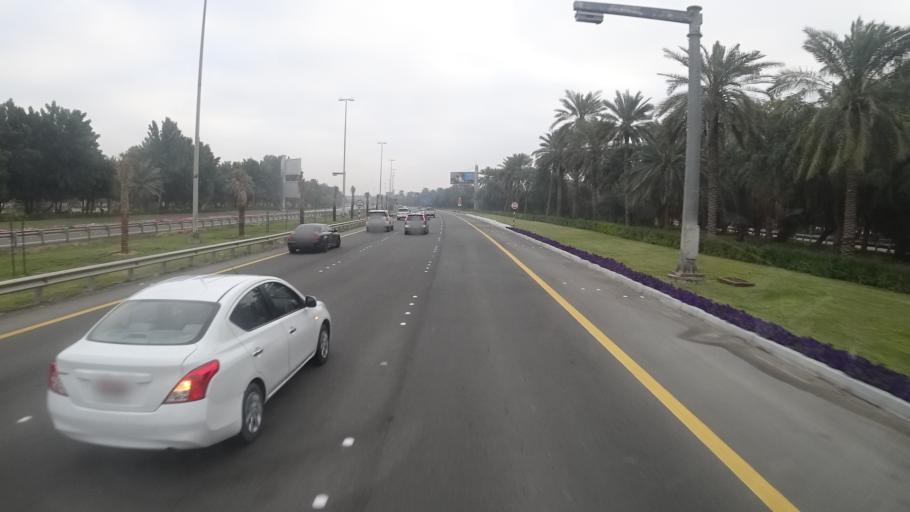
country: AE
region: Abu Dhabi
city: Abu Dhabi
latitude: 24.4081
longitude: 54.6264
